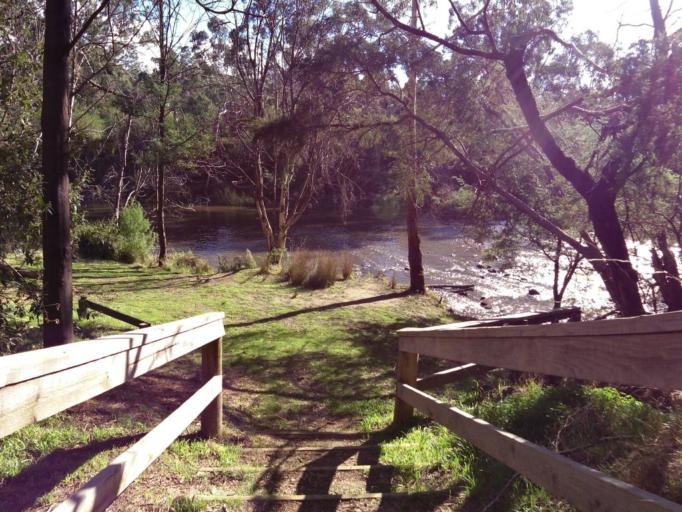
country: AU
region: Victoria
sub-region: Nillumbik
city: North Warrandyte
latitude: -37.7388
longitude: 145.1991
